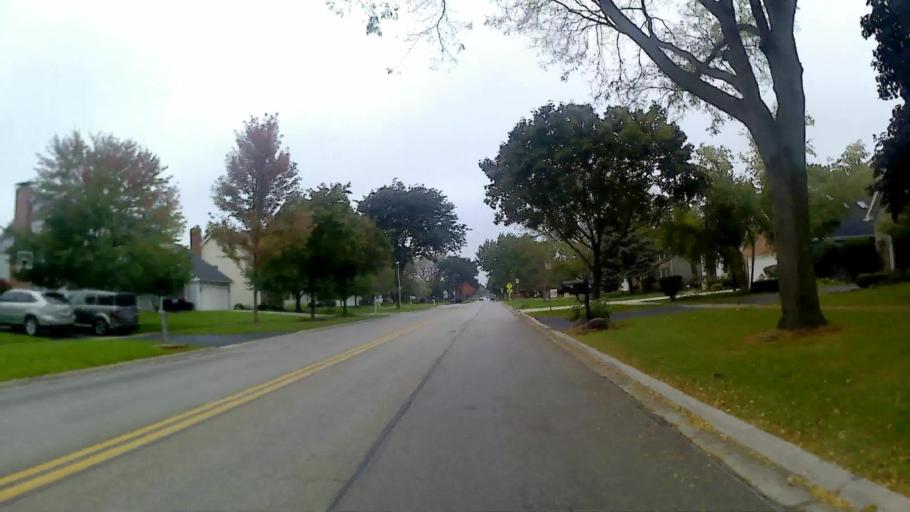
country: US
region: Illinois
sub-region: DuPage County
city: Wheaton
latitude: 41.8362
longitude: -88.1117
